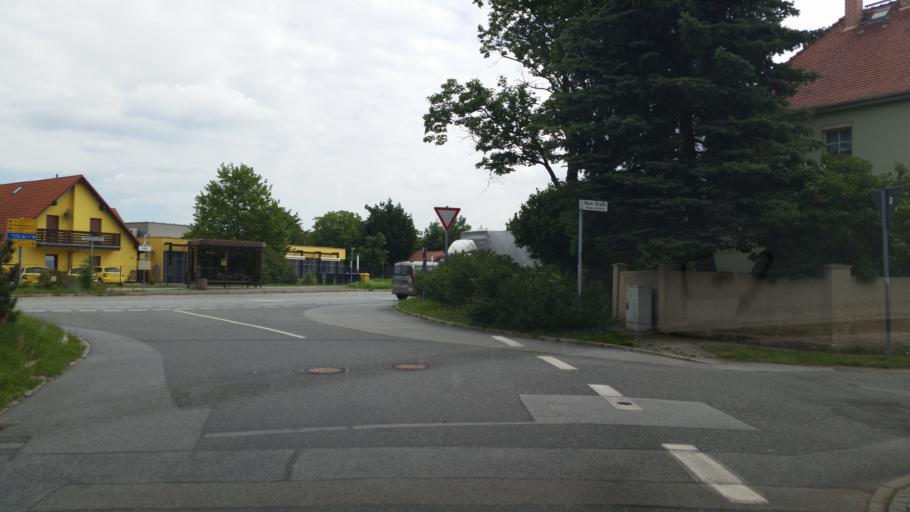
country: DE
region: Saxony
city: Radibor
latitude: 51.2131
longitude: 14.3924
